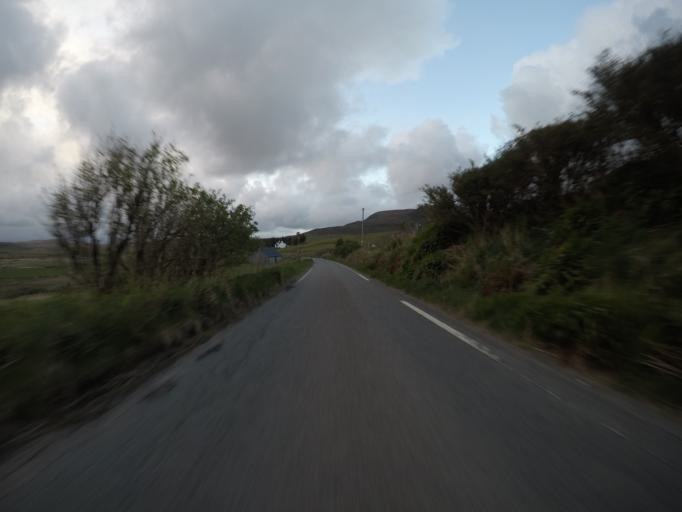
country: GB
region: Scotland
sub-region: Highland
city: Portree
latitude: 57.6126
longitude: -6.3712
